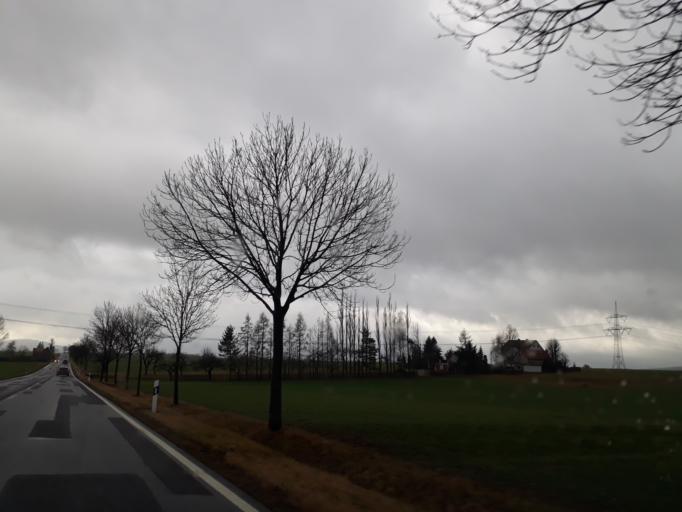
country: DE
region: Saxony
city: Herrnhut
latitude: 51.0414
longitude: 14.7084
